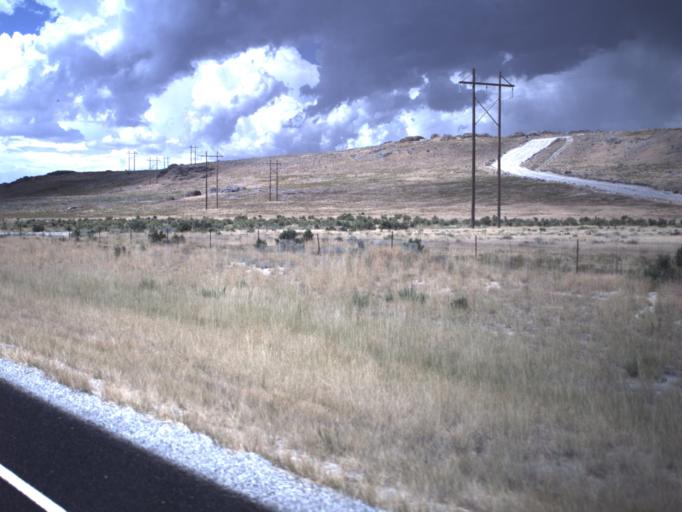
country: US
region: Utah
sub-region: Box Elder County
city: Tremonton
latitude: 41.6288
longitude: -112.4094
